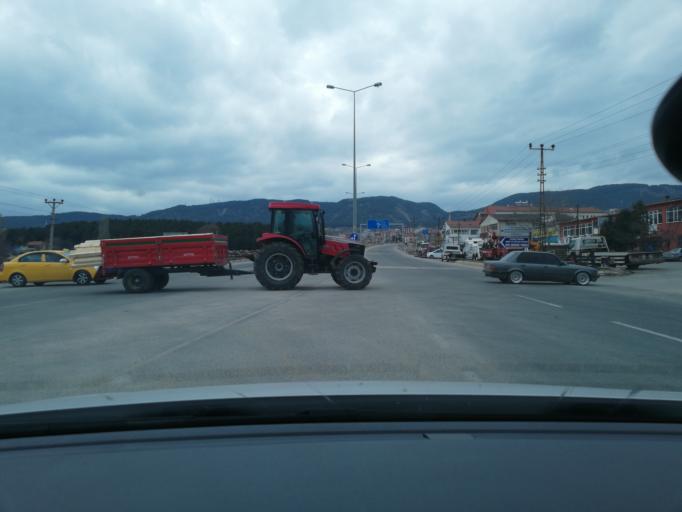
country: TR
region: Bolu
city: Gerede
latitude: 40.7879
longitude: 32.2092
